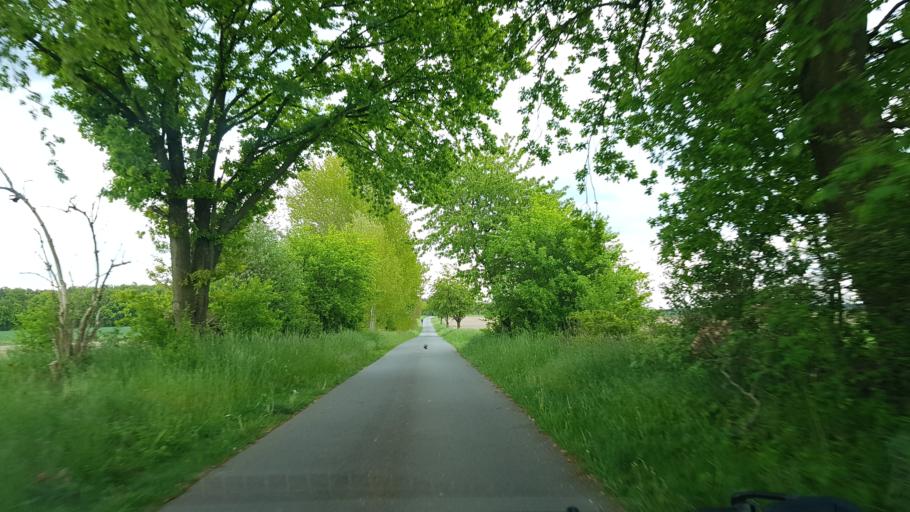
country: DE
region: Lower Saxony
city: Vastorf
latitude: 53.1925
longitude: 10.5567
